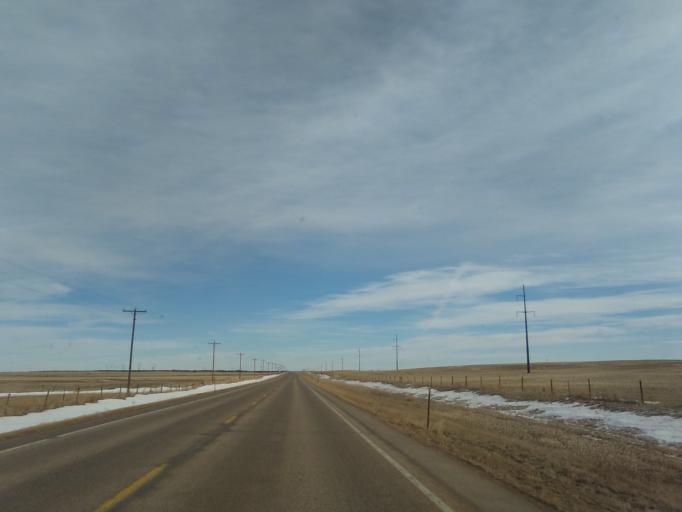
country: US
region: Wyoming
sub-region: Laramie County
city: Ranchettes
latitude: 41.4069
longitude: -104.4474
